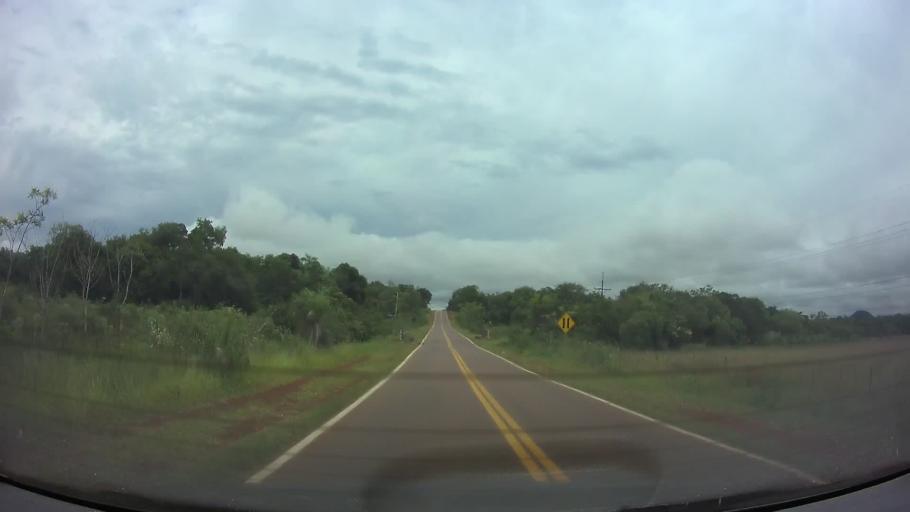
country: PY
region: Paraguari
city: Acahay
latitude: -25.8533
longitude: -57.1397
